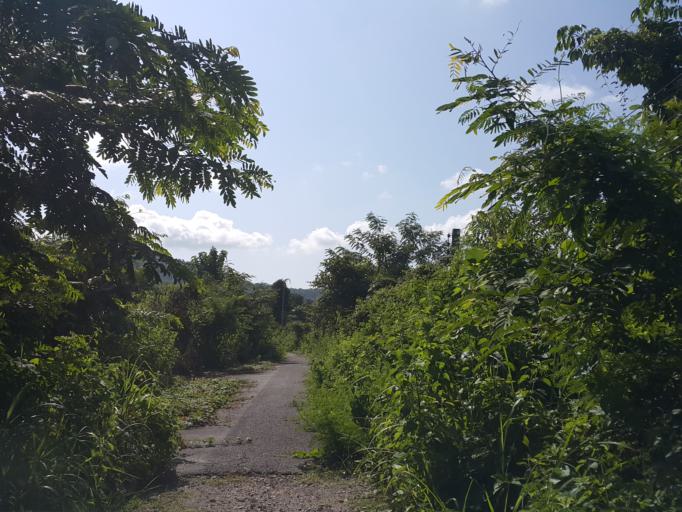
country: TH
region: Chiang Mai
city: Mae On
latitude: 18.8028
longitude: 99.1877
